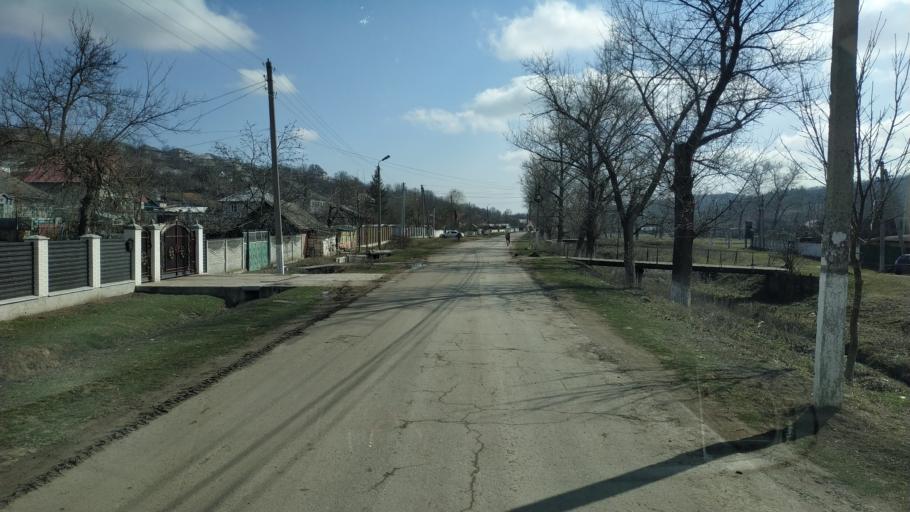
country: MD
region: Hincesti
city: Hincesti
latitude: 46.8797
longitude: 28.6255
